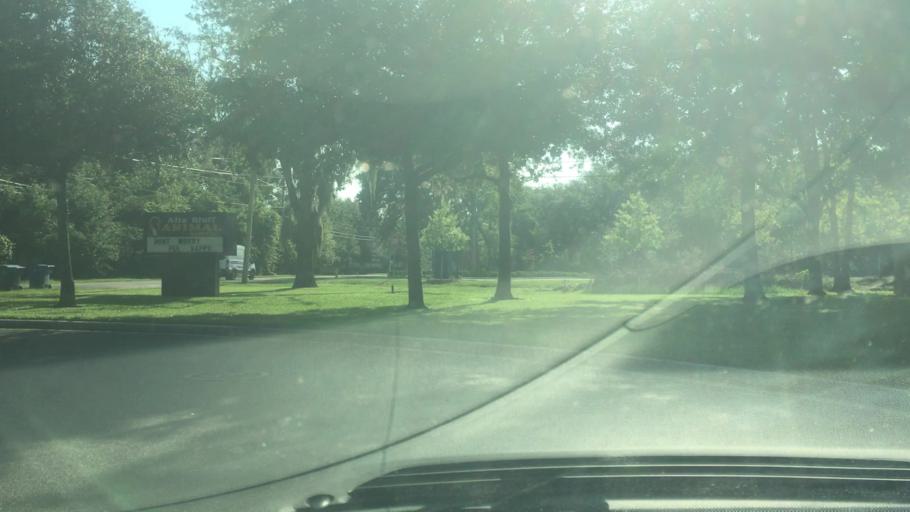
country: US
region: Florida
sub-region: Duval County
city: Jacksonville
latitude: 30.4611
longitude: -81.5773
